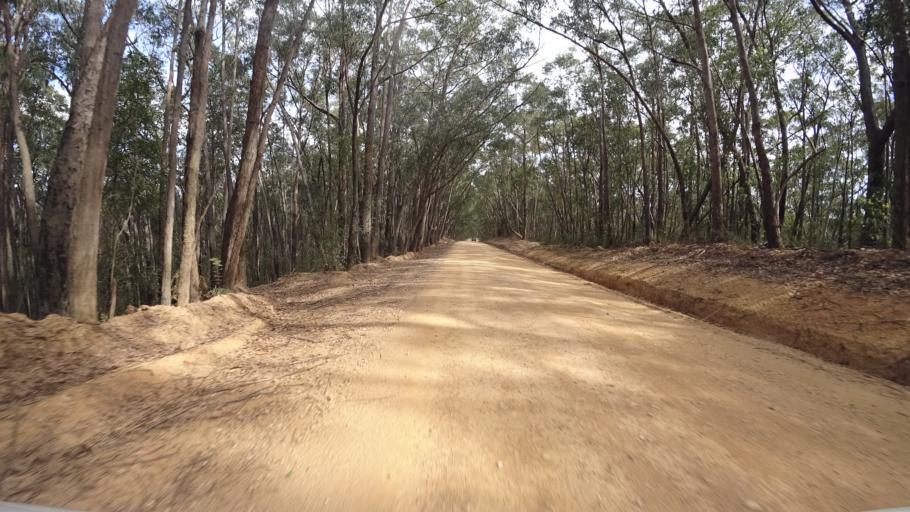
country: AU
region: New South Wales
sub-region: Shoalhaven Shire
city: Milton
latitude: -35.3529
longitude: 150.2168
